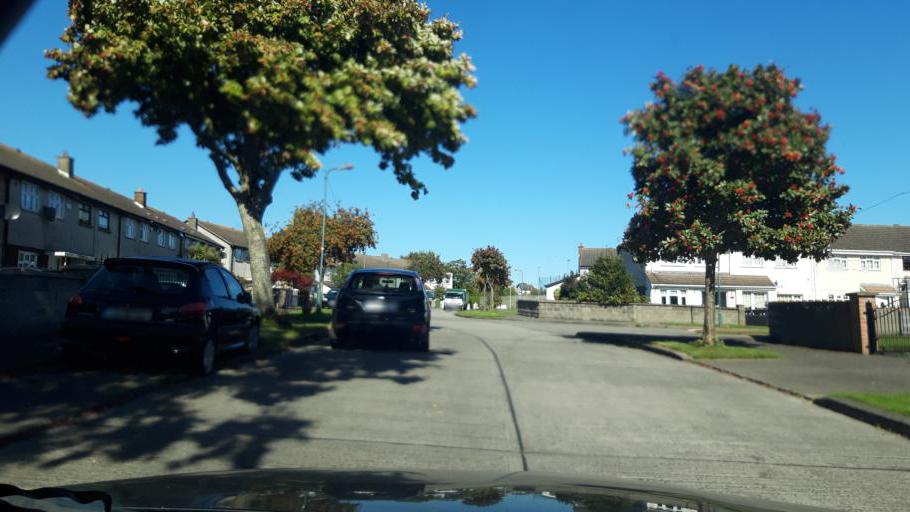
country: IE
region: Leinster
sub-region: Dublin City
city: Finglas
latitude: 53.3835
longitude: -6.3207
